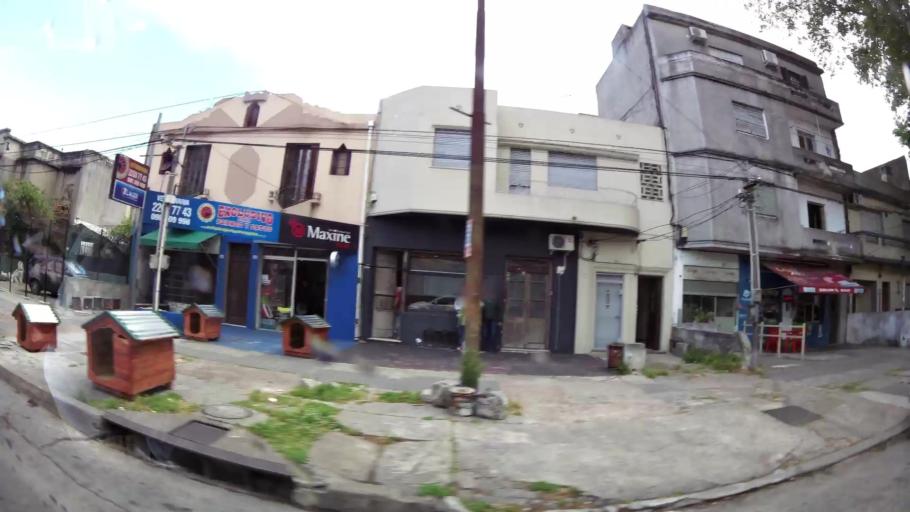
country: UY
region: Montevideo
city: Montevideo
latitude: -34.8656
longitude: -56.1803
